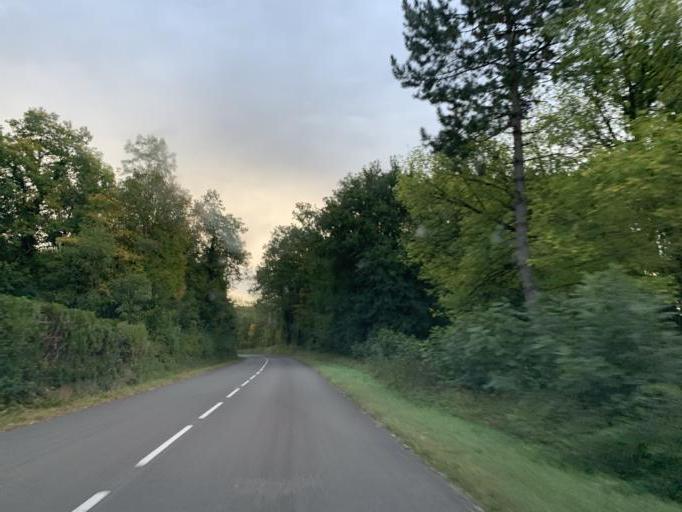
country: FR
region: Rhone-Alpes
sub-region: Departement de l'Isere
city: Les Avenieres
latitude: 45.7086
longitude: 5.5626
